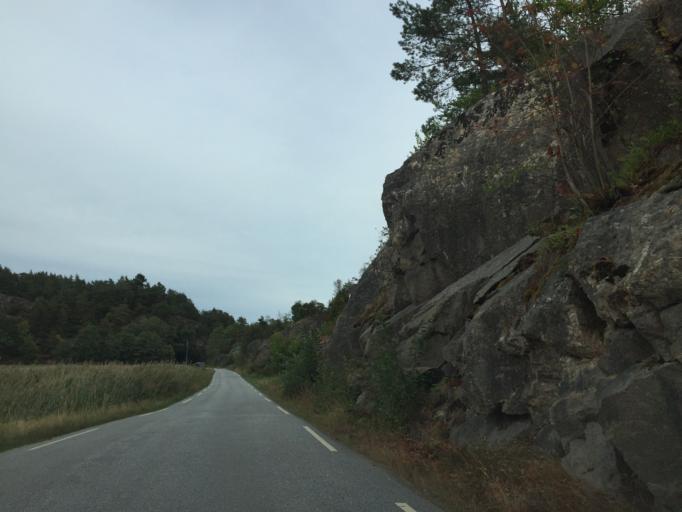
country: NO
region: Ostfold
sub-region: Hvaler
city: Skjaerhalden
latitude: 59.0707
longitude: 11.0816
